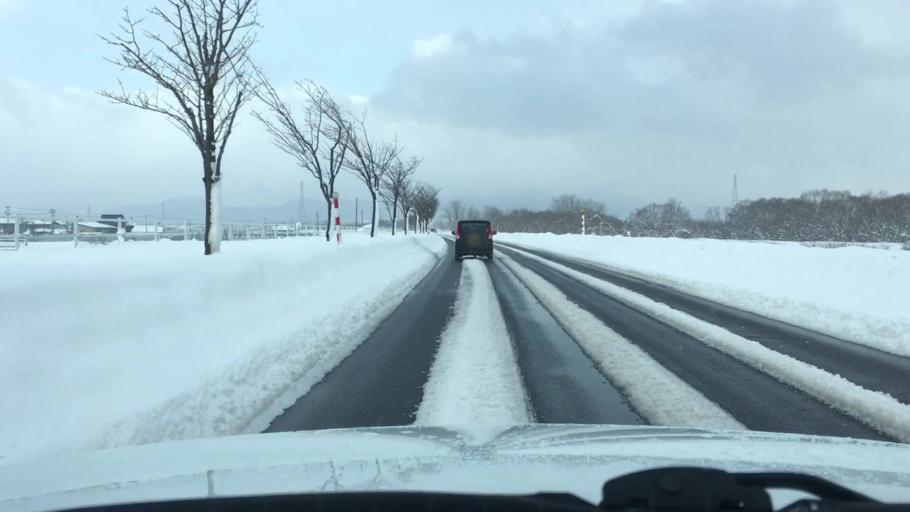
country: JP
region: Aomori
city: Hirosaki
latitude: 40.6367
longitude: 140.4717
